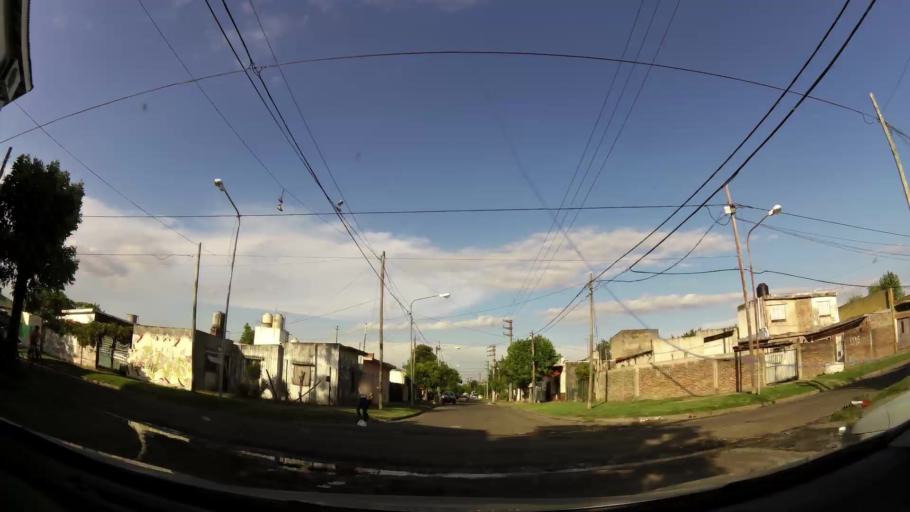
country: AR
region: Buenos Aires
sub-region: Partido de Tigre
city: Tigre
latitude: -34.4660
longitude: -58.6594
